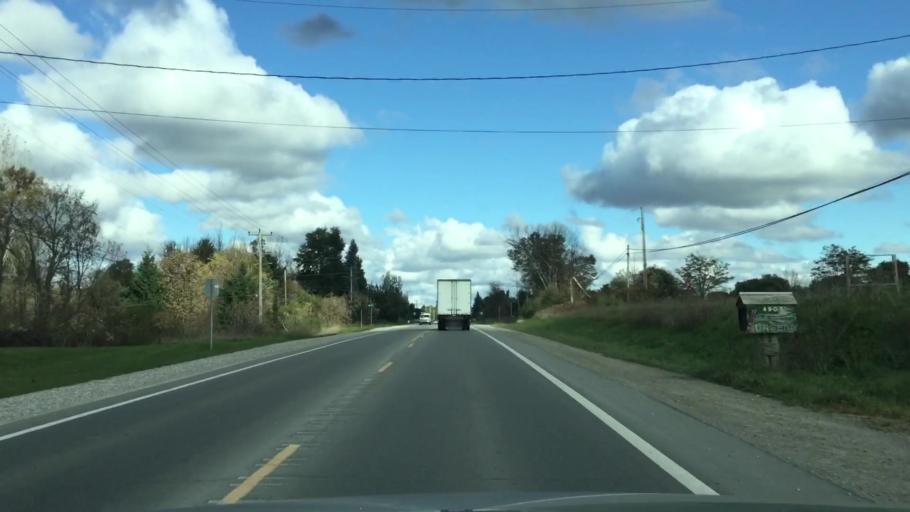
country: US
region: Michigan
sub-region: Oakland County
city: Oxford
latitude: 42.9145
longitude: -83.3125
